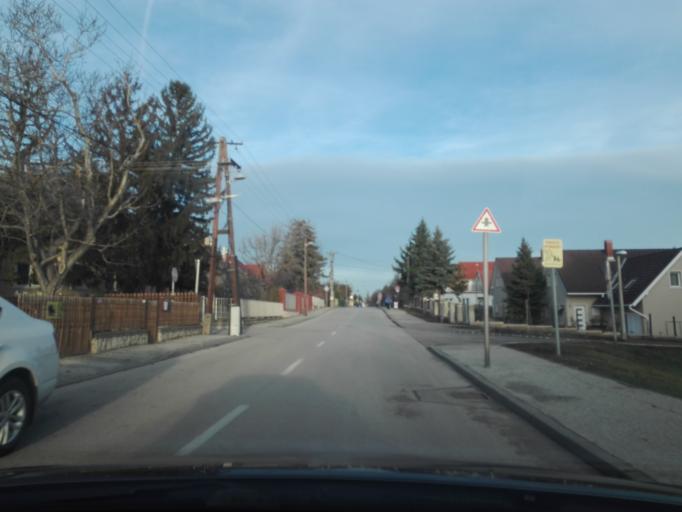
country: HU
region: Veszprem
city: Balatonfured
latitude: 46.9578
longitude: 17.8758
